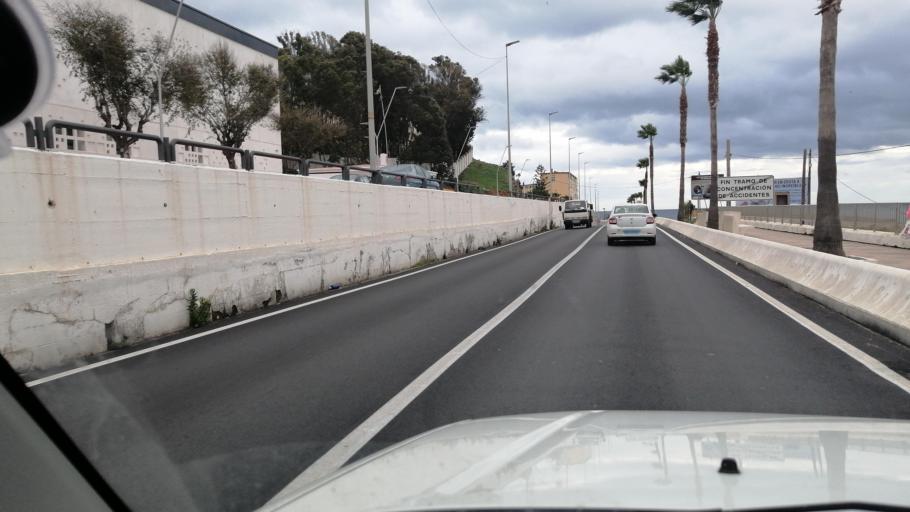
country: ES
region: Ceuta
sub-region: Ceuta
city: Ceuta
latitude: 35.8796
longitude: -5.3321
